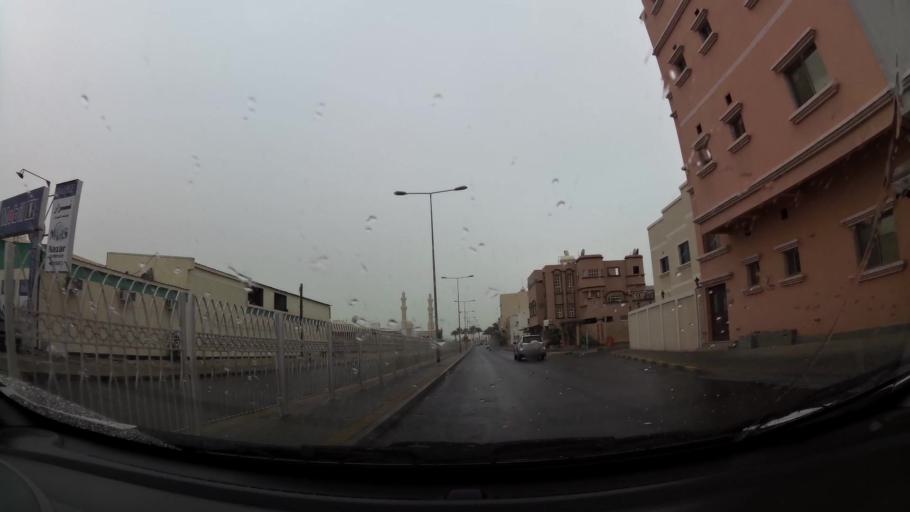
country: BH
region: Northern
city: Madinat `Isa
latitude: 26.1719
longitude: 50.5525
